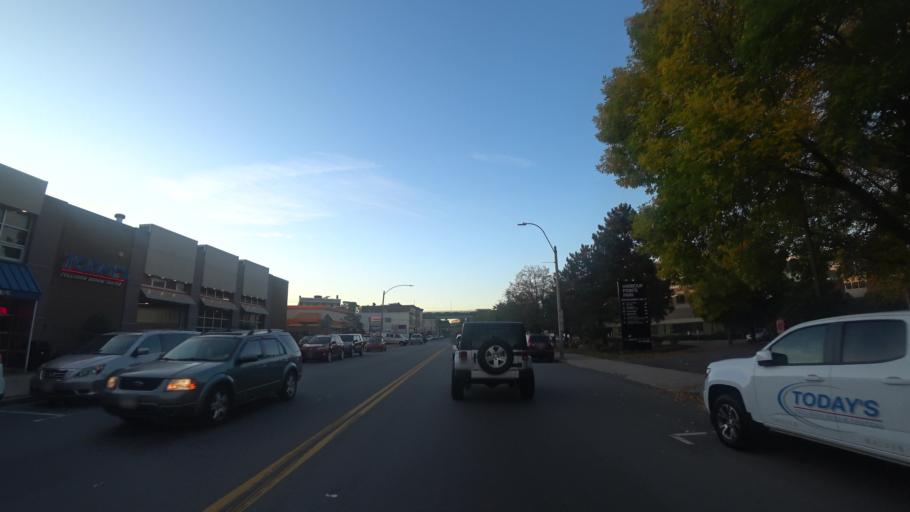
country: US
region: Massachusetts
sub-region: Suffolk County
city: Chelsea
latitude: 42.3943
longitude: -71.0394
